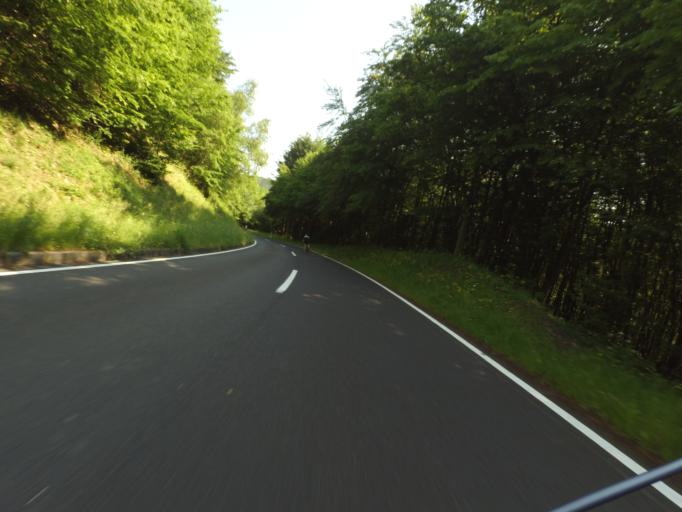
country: DE
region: Rheinland-Pfalz
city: Roes
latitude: 50.2483
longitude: 7.2682
